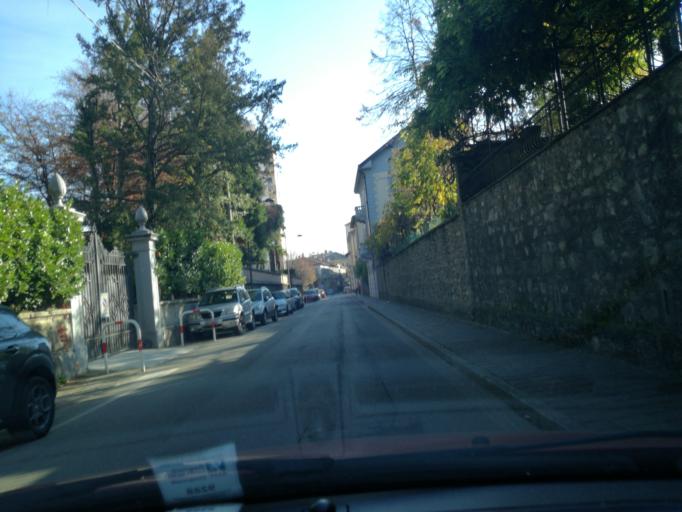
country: IT
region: Lombardy
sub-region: Provincia di Lecco
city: Merate
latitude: 45.6992
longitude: 9.4123
